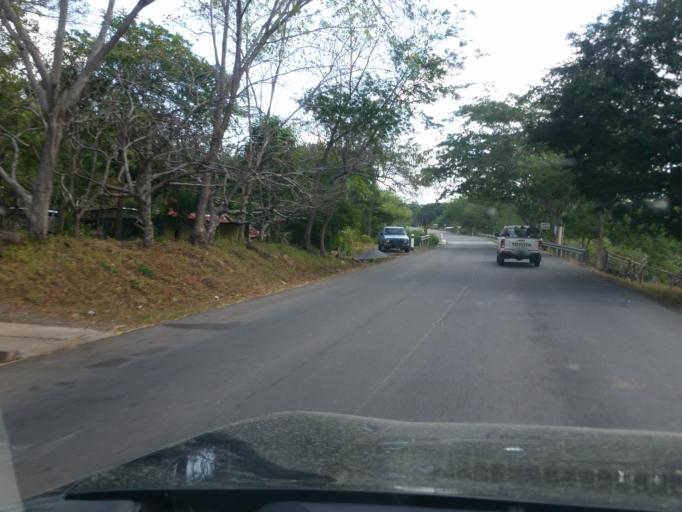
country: NI
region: Chontales
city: Comalapa
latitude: 12.1919
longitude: -85.6147
